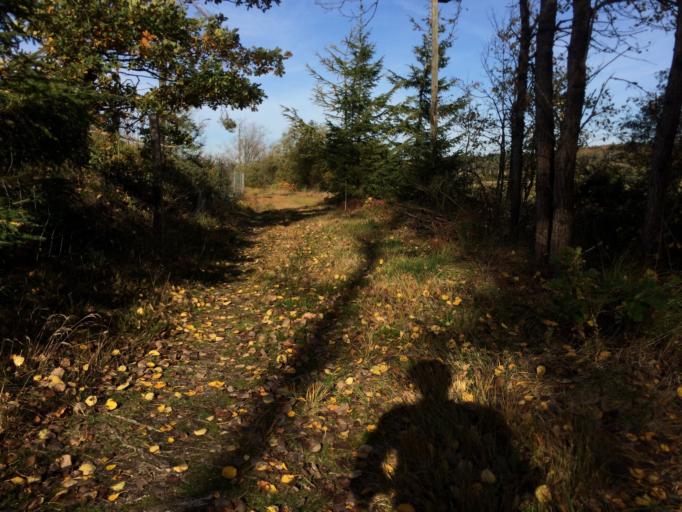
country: DK
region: Central Jutland
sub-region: Holstebro Kommune
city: Ulfborg
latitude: 56.2763
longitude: 8.4710
